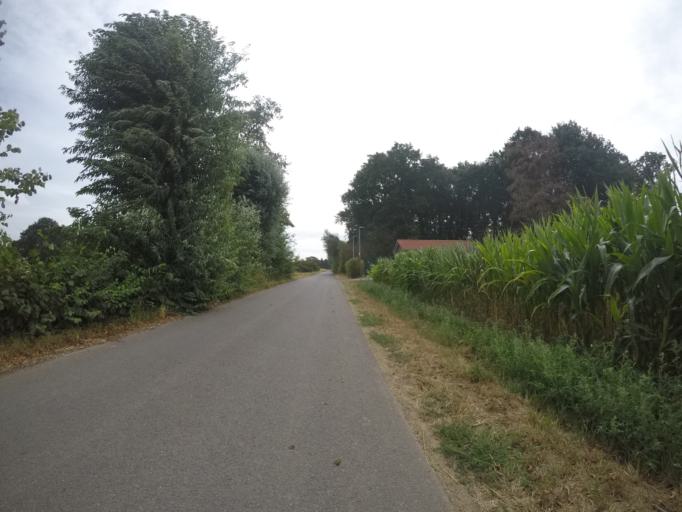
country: DE
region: North Rhine-Westphalia
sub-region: Regierungsbezirk Dusseldorf
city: Bocholt
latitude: 51.8577
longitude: 6.5709
